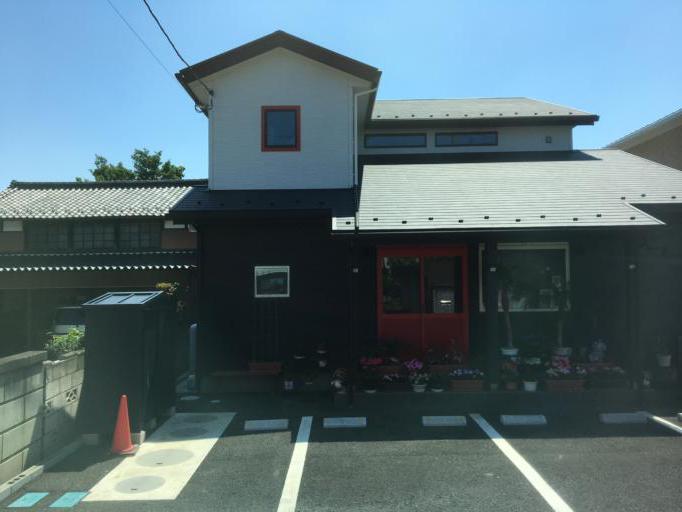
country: JP
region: Saitama
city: Kawagoe
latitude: 35.9439
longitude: 139.4872
